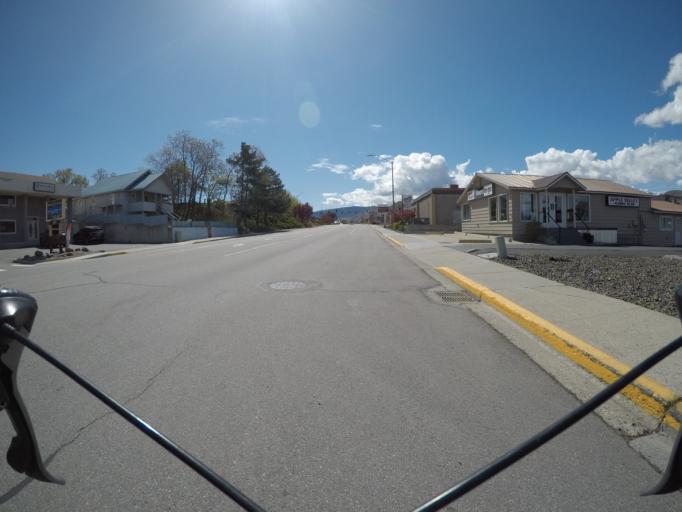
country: US
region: Washington
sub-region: Douglas County
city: East Wenatchee
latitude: 47.4137
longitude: -120.2923
